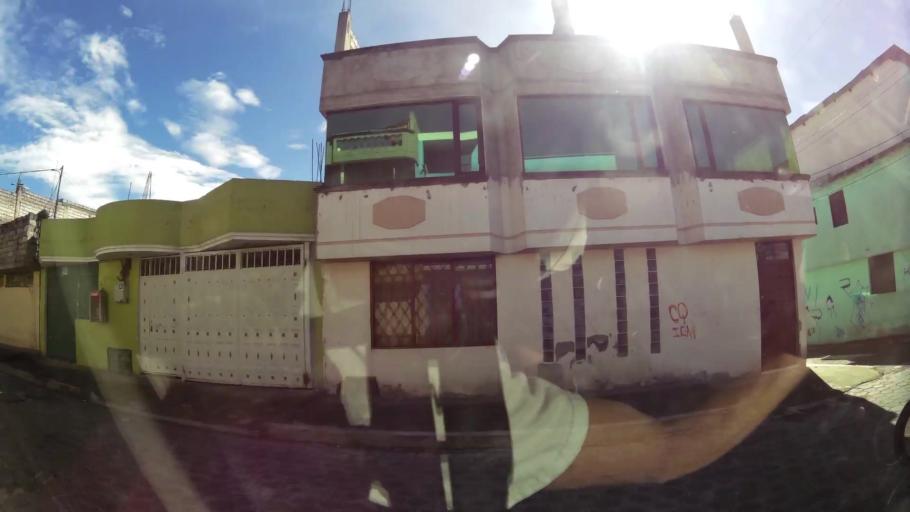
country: EC
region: Pichincha
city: Quito
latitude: -0.3015
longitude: -78.5621
